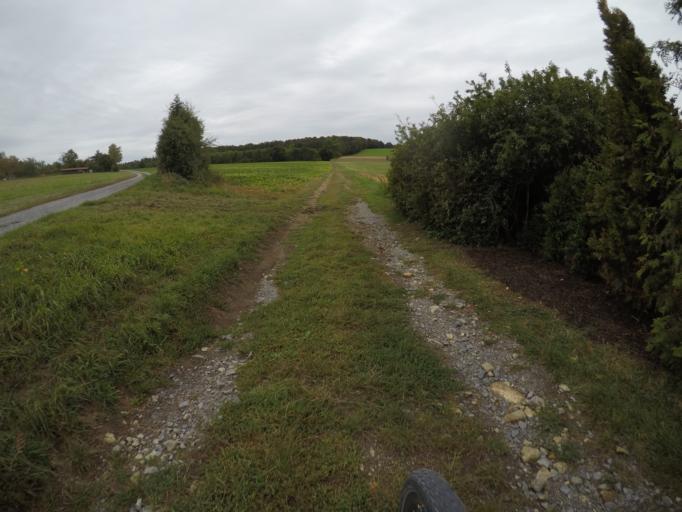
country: DE
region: Baden-Wuerttemberg
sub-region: Regierungsbezirk Stuttgart
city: Eberdingen
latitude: 48.8806
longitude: 8.9854
